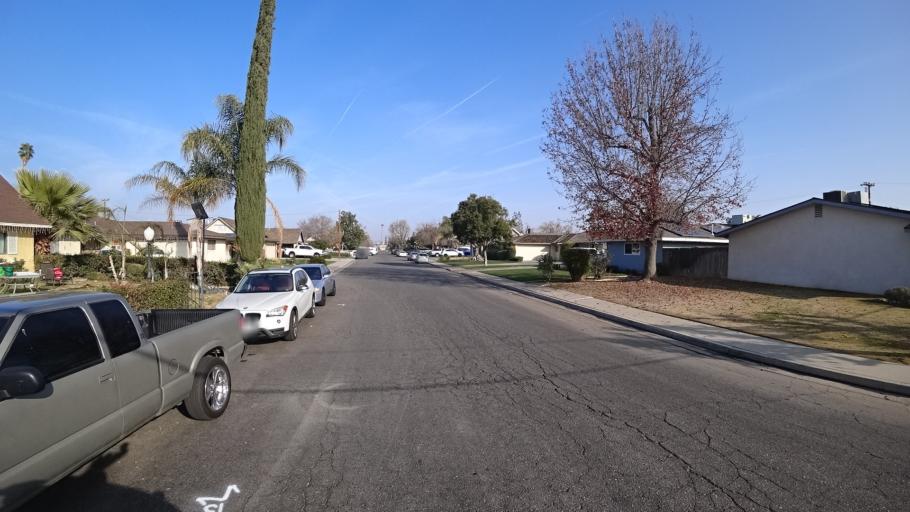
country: US
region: California
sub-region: Kern County
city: Bakersfield
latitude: 35.3273
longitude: -119.0322
